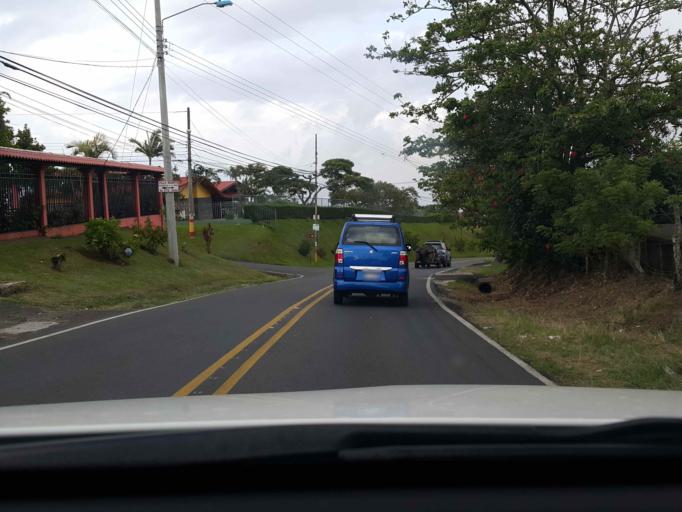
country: CR
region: Heredia
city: San Josecito
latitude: 10.0317
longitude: -84.0918
